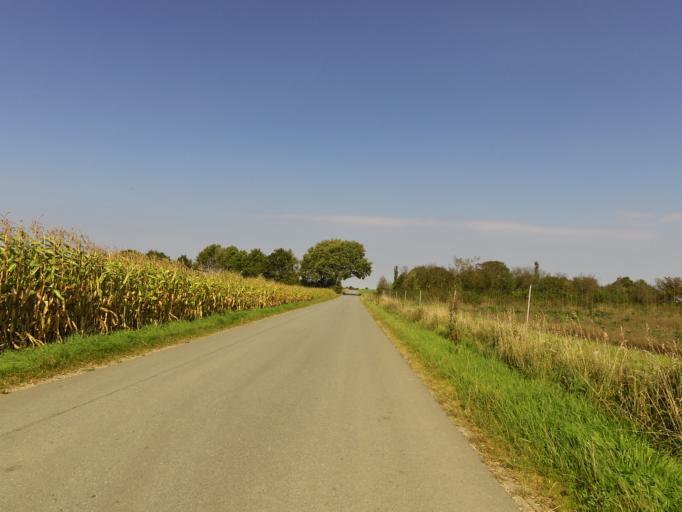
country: DK
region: South Denmark
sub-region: Vejen Kommune
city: Rodding
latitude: 55.3879
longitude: 9.1398
